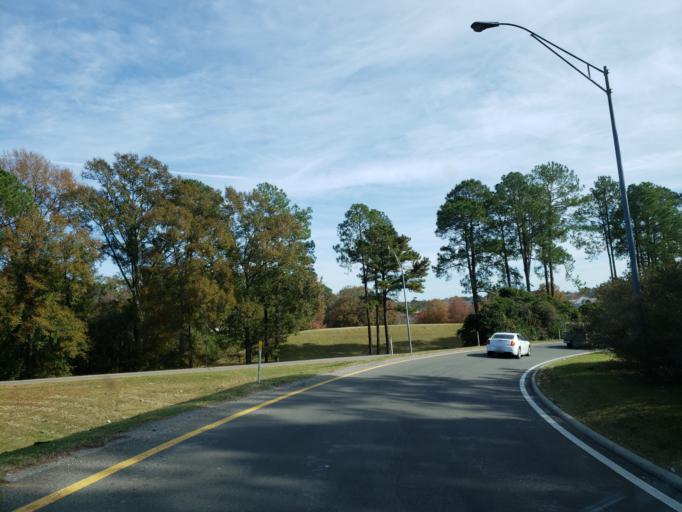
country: US
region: Mississippi
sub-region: Forrest County
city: Rawls Springs
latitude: 31.3574
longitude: -89.3450
